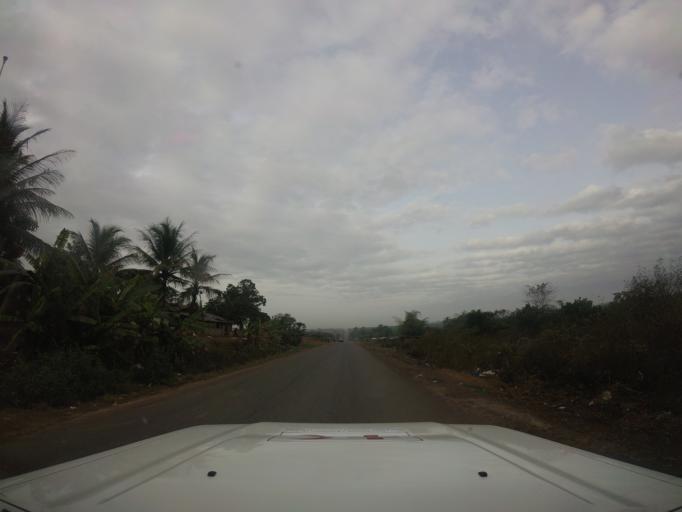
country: LR
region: Bomi
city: Tubmanburg
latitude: 6.7309
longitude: -11.0069
